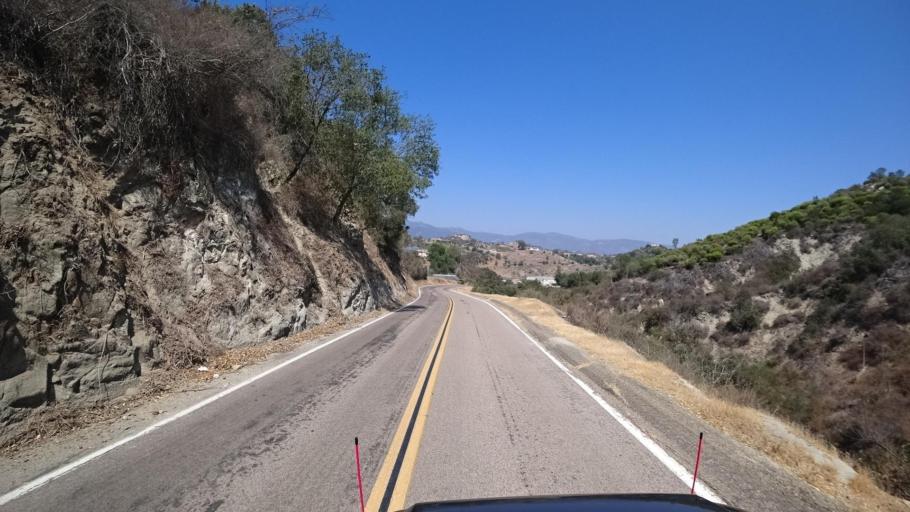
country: US
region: California
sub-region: San Diego County
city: Fallbrook
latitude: 33.4188
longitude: -117.3038
